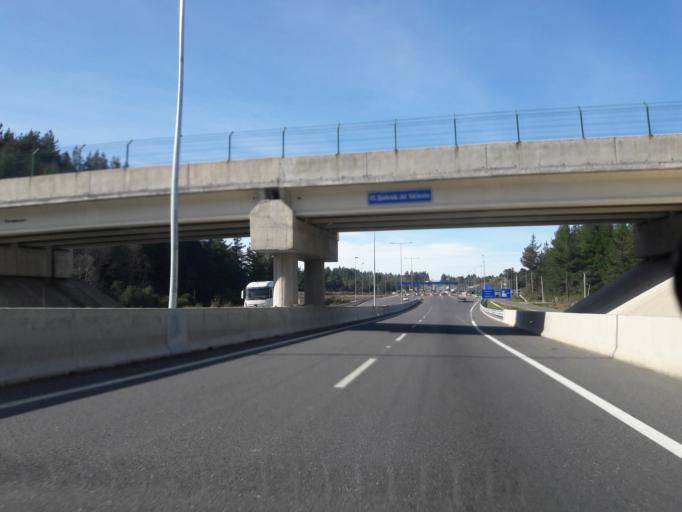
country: CL
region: Biobio
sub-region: Provincia de Biobio
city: Yumbel
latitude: -36.9597
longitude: -72.7323
